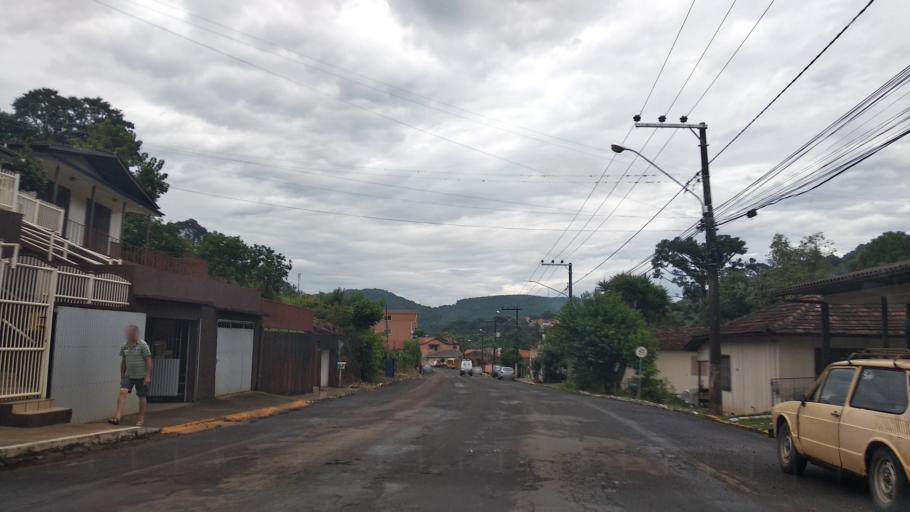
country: BR
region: Santa Catarina
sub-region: Videira
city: Videira
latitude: -27.0981
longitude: -51.2493
